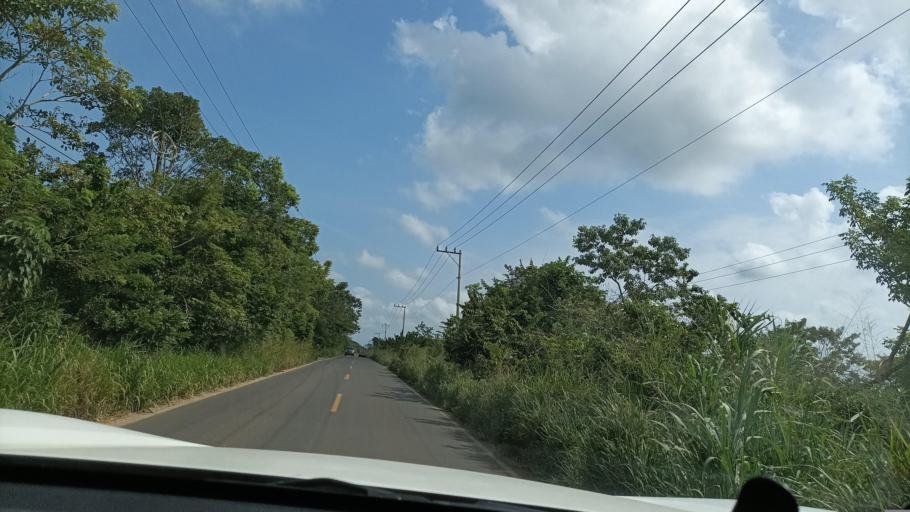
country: MX
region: Veracruz
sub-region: Chinameca
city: Chacalapa
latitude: 18.0718
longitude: -94.6894
